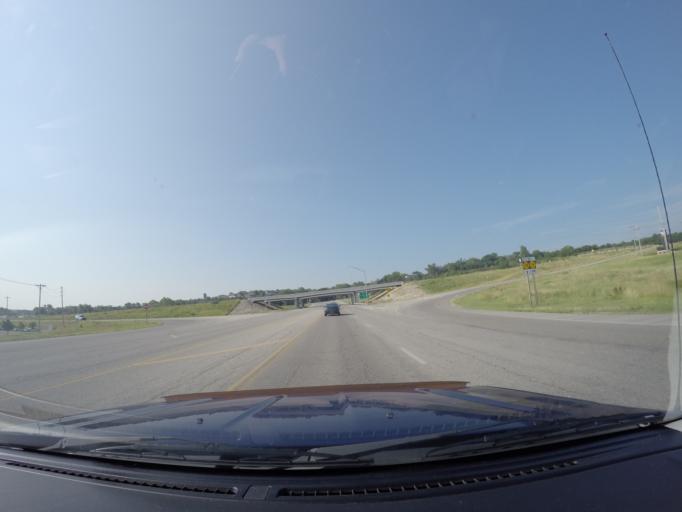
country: US
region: Kansas
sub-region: Riley County
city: Manhattan
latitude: 39.1704
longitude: -96.6038
